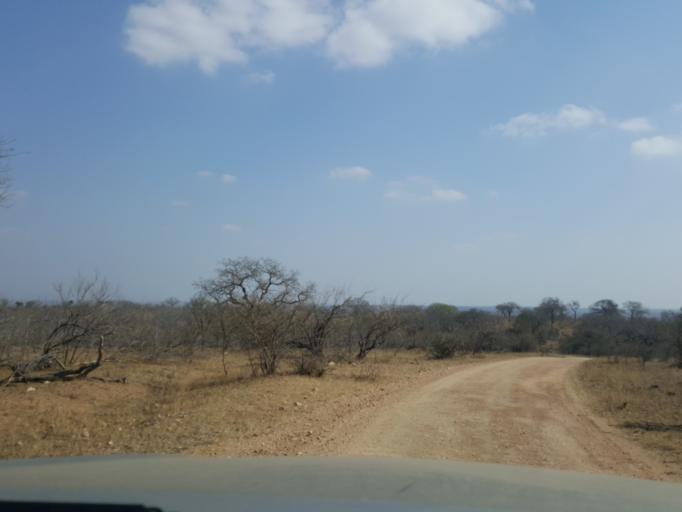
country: ZA
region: Mpumalanga
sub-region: Ehlanzeni District
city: Komatipoort
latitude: -25.2710
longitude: 31.7946
